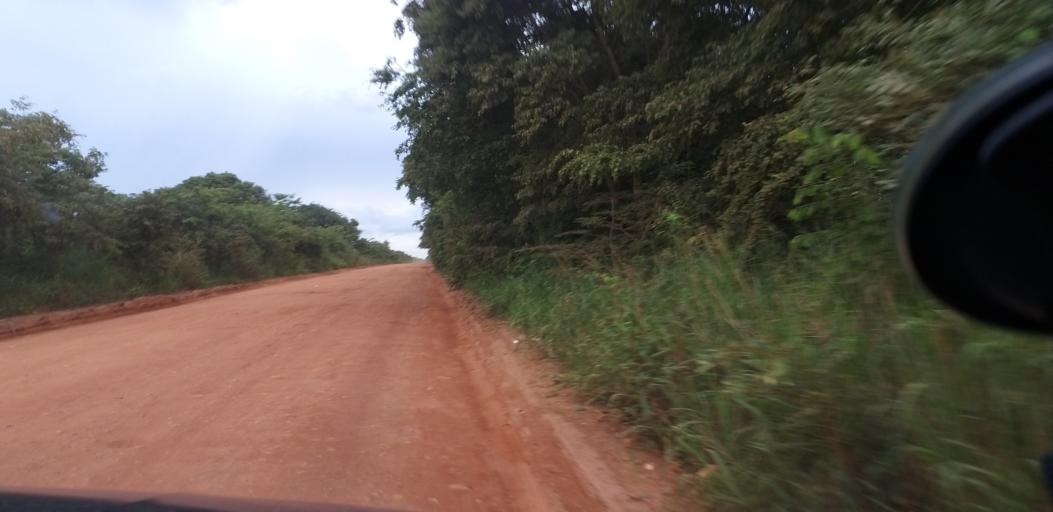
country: ZM
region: Lusaka
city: Lusaka
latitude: -15.2072
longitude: 28.4363
